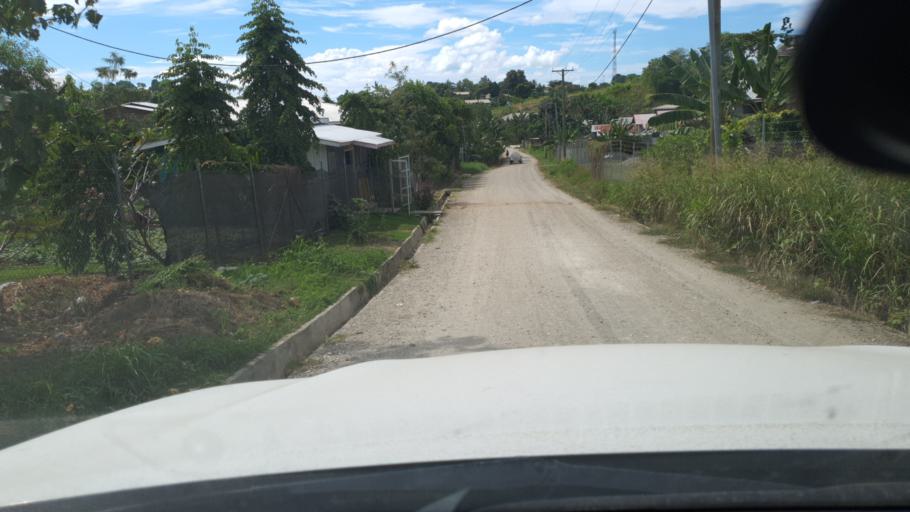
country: SB
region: Guadalcanal
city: Honiara
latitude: -9.4487
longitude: 159.9753
